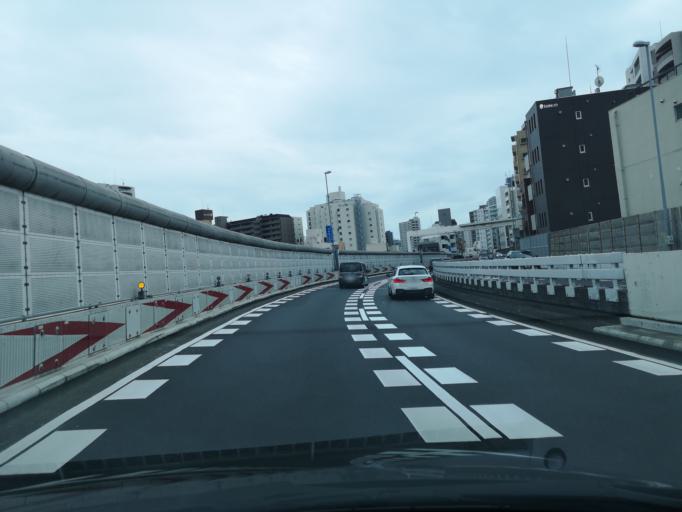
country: JP
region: Tokyo
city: Tokyo
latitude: 35.6505
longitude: 139.7375
